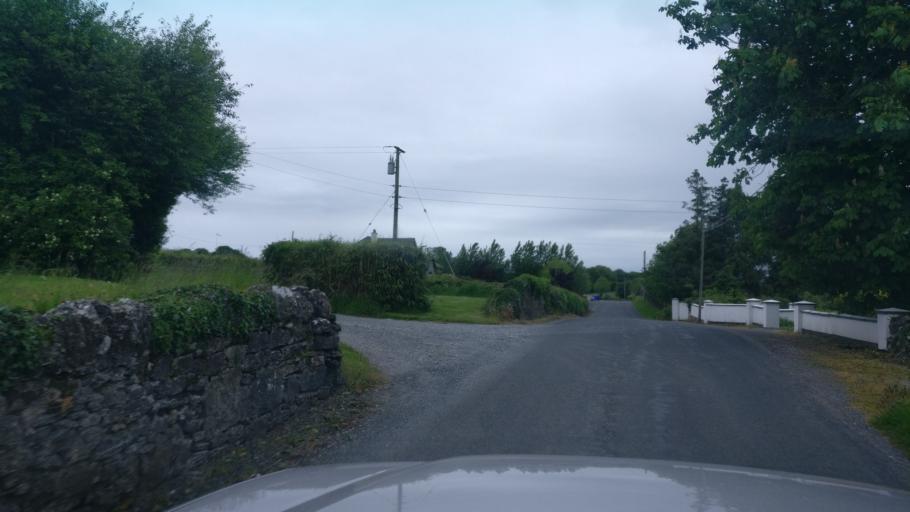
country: IE
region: Connaught
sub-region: County Galway
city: Loughrea
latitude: 53.1121
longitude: -8.4105
